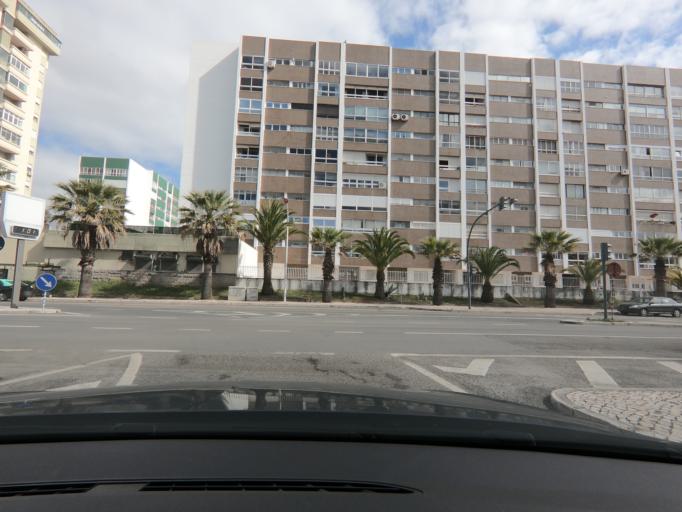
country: PT
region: Lisbon
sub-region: Cascais
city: Sao Domingos de Rana
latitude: 38.6954
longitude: -9.3283
